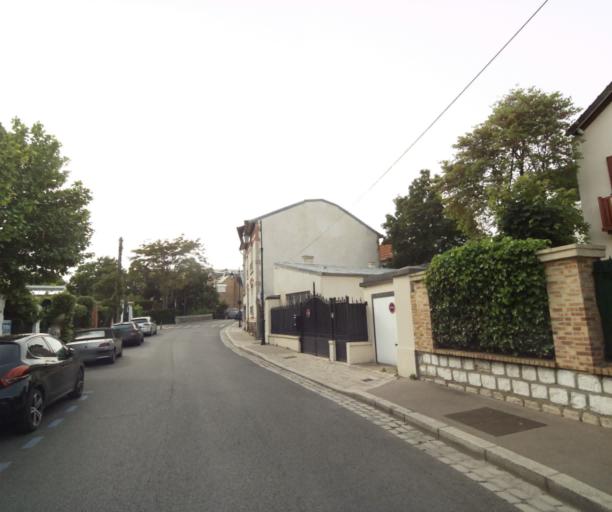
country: FR
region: Ile-de-France
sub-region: Departement des Hauts-de-Seine
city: Colombes
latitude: 48.9195
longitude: 2.2618
